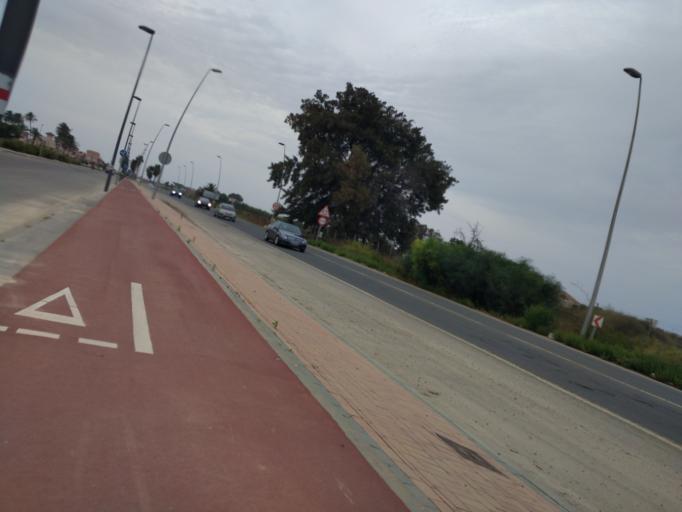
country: ES
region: Murcia
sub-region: Murcia
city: Los Alcazares
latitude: 37.7235
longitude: -0.8615
